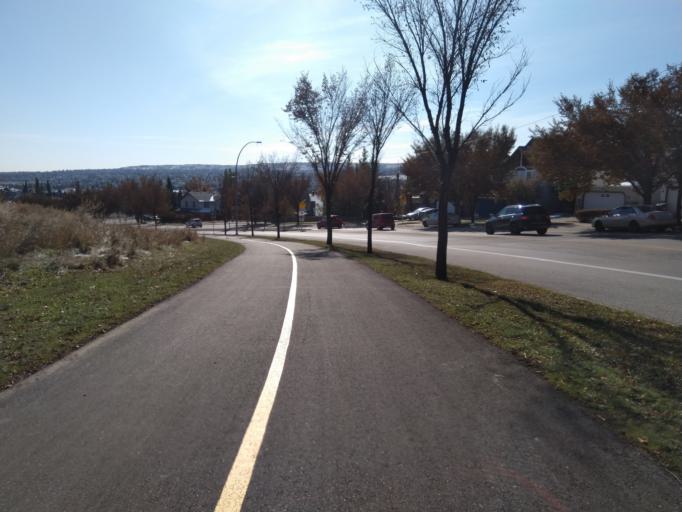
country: CA
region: Alberta
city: Calgary
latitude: 51.1583
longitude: -114.1015
